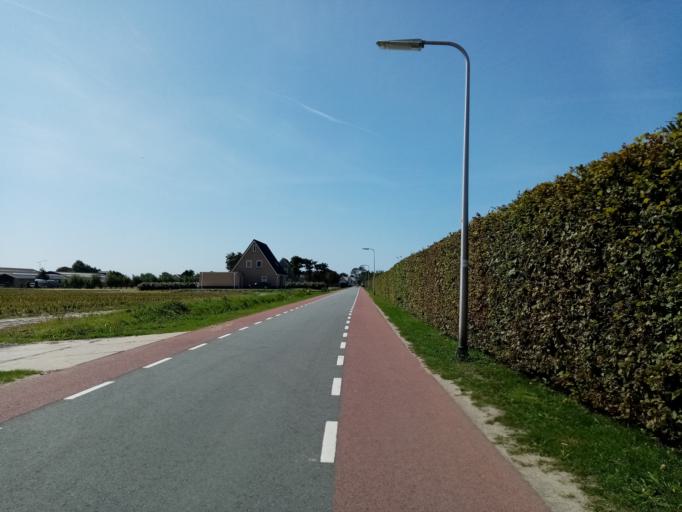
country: NL
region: South Holland
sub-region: Gemeente Noordwijkerhout
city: Noordwijkerhout
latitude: 52.2697
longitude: 4.4748
